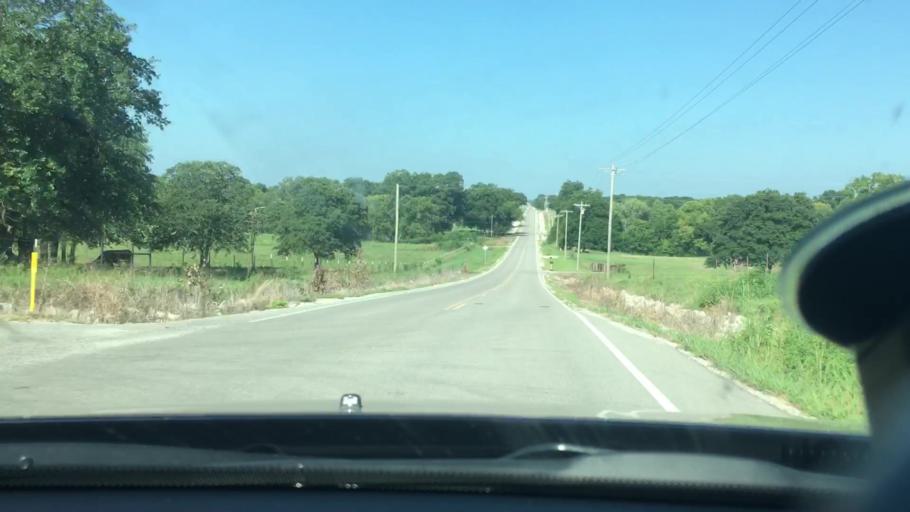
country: US
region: Oklahoma
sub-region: Love County
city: Marietta
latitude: 34.0275
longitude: -97.1607
